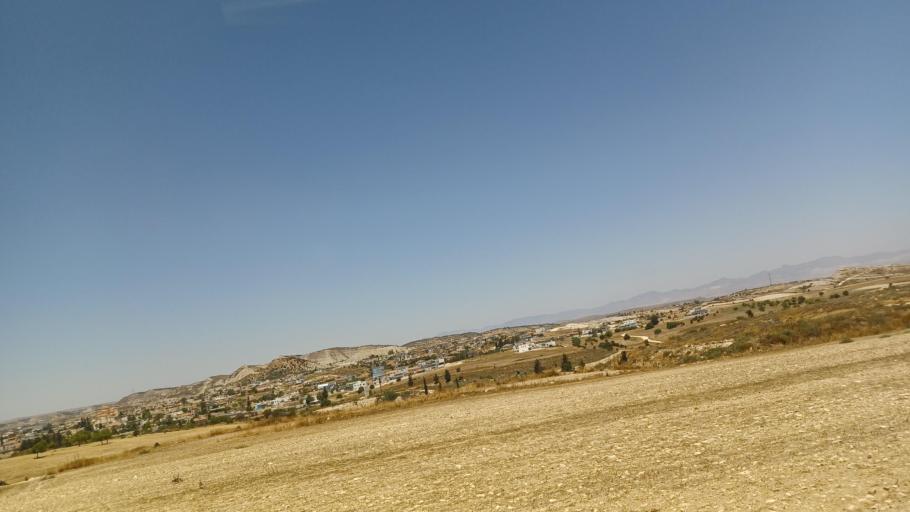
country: CY
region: Lefkosia
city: Lympia
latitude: 34.9905
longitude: 33.4781
